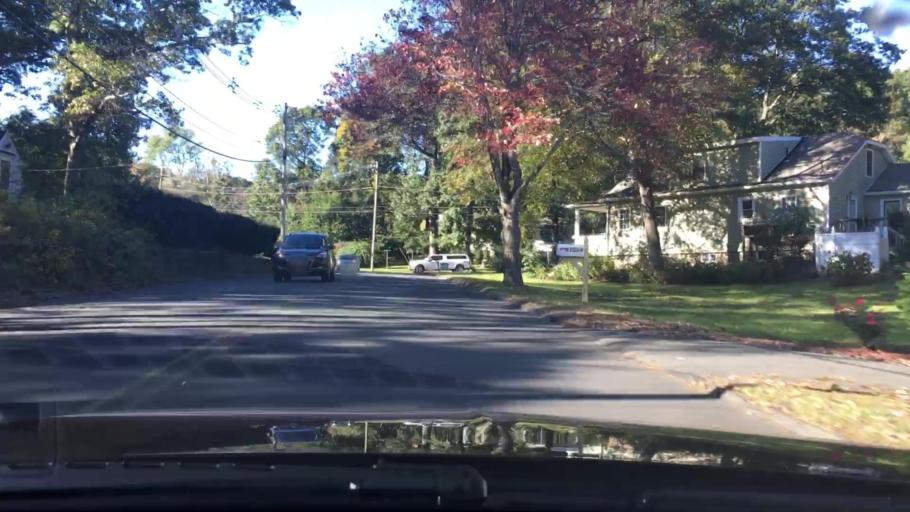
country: US
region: Connecticut
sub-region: New Haven County
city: Prospect
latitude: 41.5484
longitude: -72.9586
